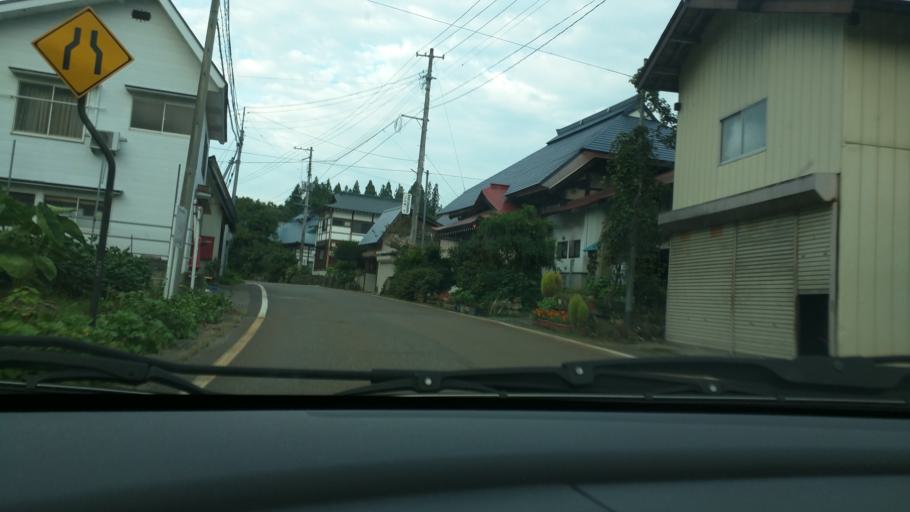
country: JP
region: Fukushima
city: Kitakata
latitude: 37.4391
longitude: 139.6827
